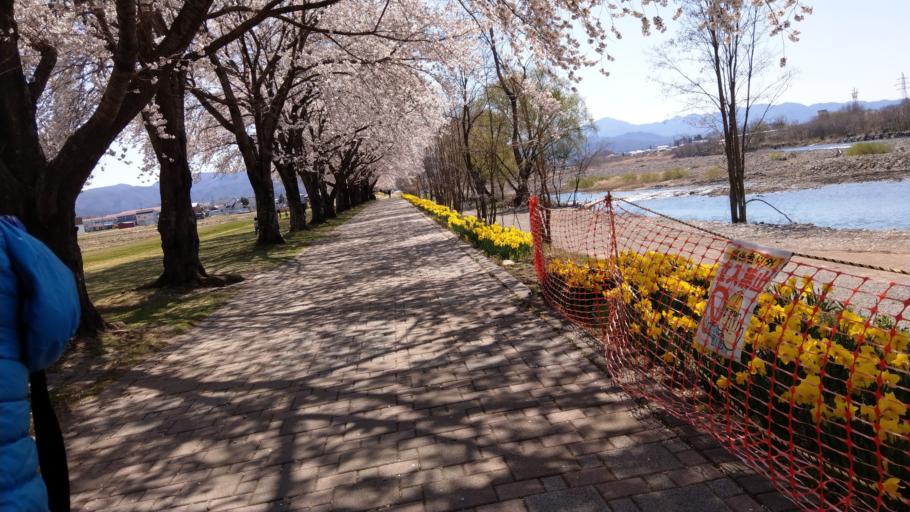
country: JP
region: Nagano
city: Saku
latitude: 36.2384
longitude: 138.4645
